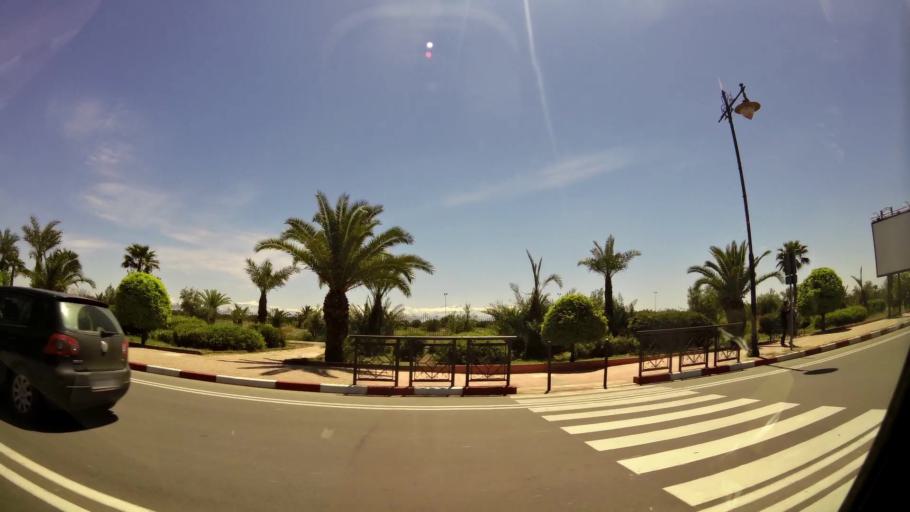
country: MA
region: Marrakech-Tensift-Al Haouz
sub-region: Marrakech
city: Marrakesh
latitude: 31.6151
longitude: -8.0147
